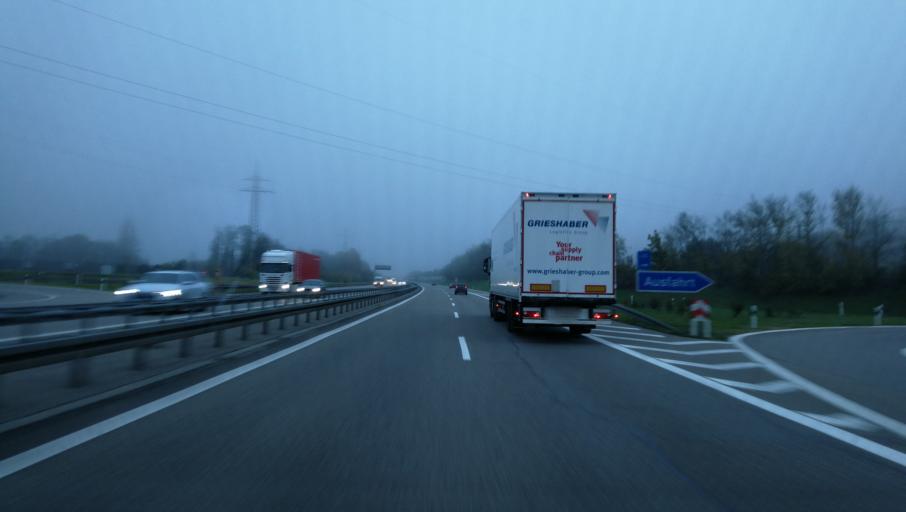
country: FR
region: Alsace
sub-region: Departement du Haut-Rhin
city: Kembs
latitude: 47.6783
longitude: 7.5235
